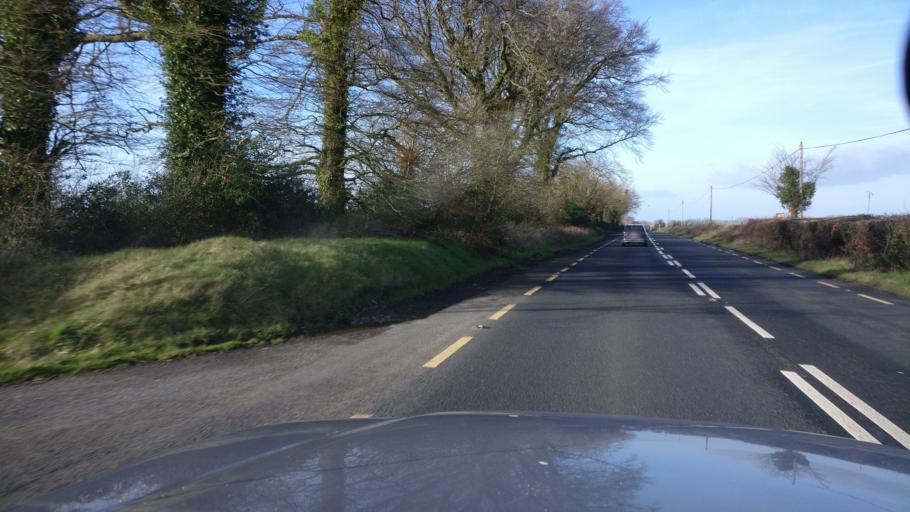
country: IE
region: Leinster
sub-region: Uibh Fhaili
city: Tullamore
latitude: 53.2027
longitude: -7.4330
